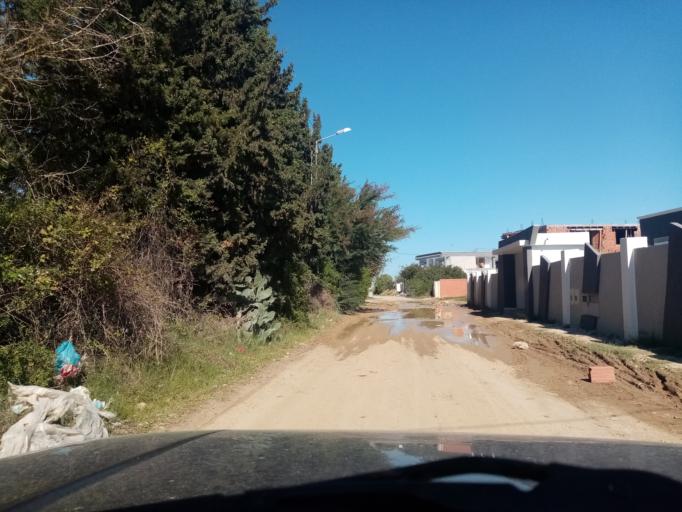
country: TN
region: Nabul
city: Bu `Urqub
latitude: 36.5780
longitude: 10.5711
